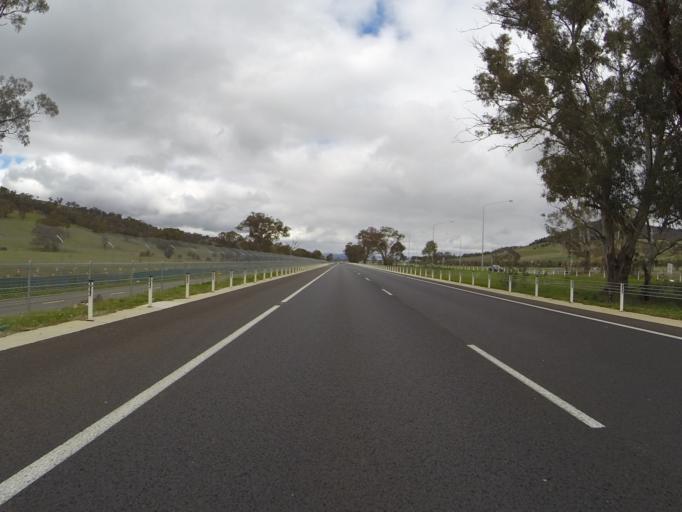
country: AU
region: Australian Capital Territory
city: Kaleen
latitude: -35.2218
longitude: 149.1961
